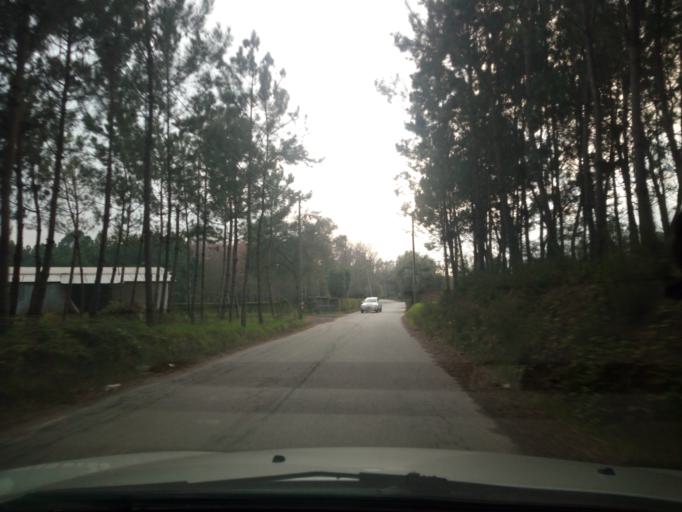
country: PT
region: Aveiro
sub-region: Oliveira do Bairro
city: Oliveira do Bairro
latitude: 40.5521
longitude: -8.4771
